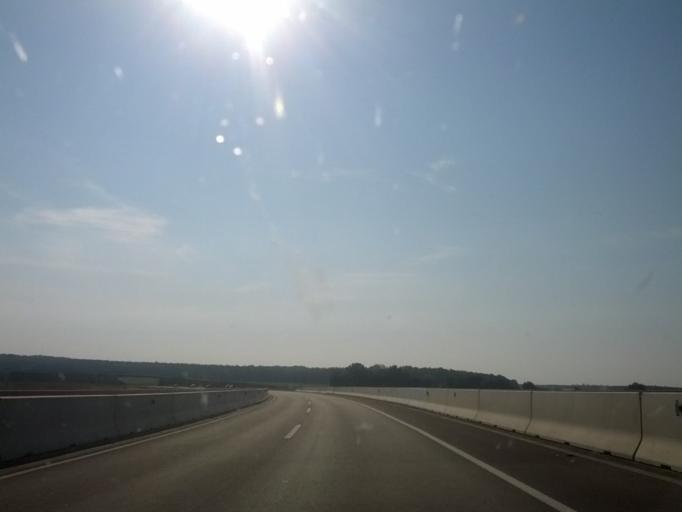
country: DE
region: Brandenburg
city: Ahrensfelde
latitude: 52.6136
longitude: 13.5634
